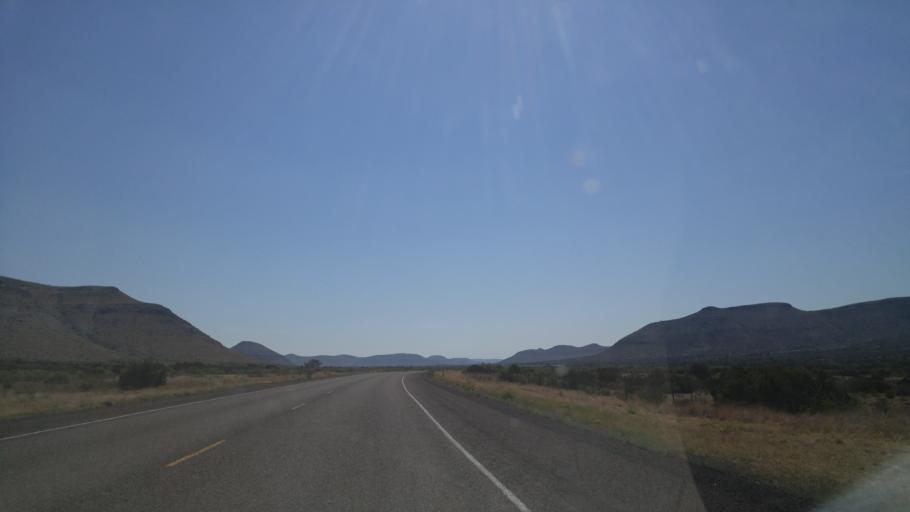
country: US
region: Texas
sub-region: Terrell County
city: Sanderson
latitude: 30.1783
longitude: -102.7815
